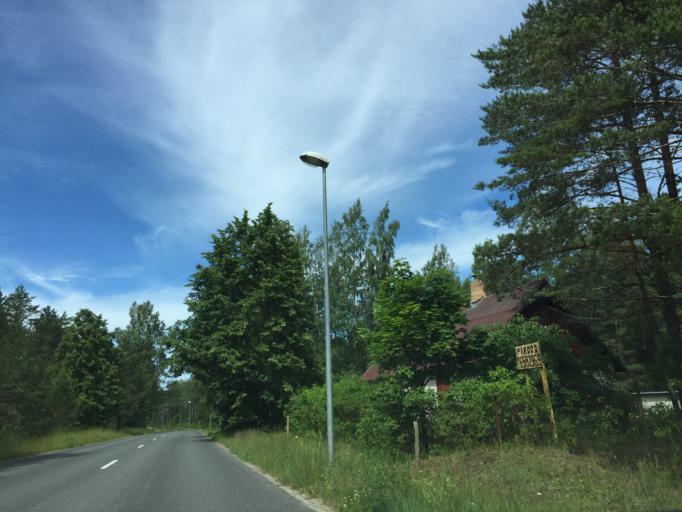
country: LV
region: Dundaga
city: Dundaga
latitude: 57.6543
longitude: 22.5726
